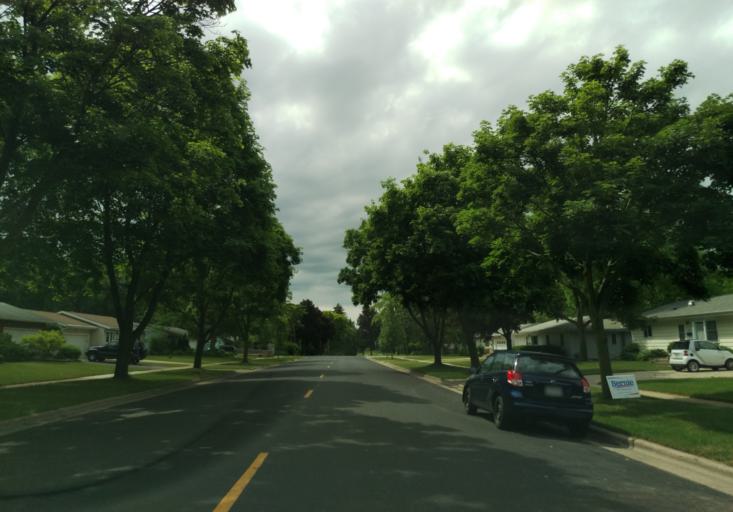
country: US
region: Wisconsin
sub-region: Dane County
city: Shorewood Hills
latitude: 43.0288
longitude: -89.4760
